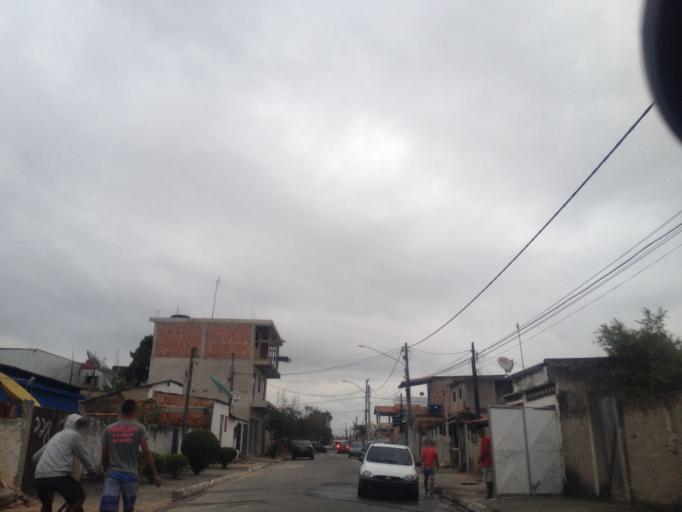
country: BR
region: Rio de Janeiro
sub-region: Porto Real
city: Porto Real
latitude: -22.4087
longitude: -44.2985
